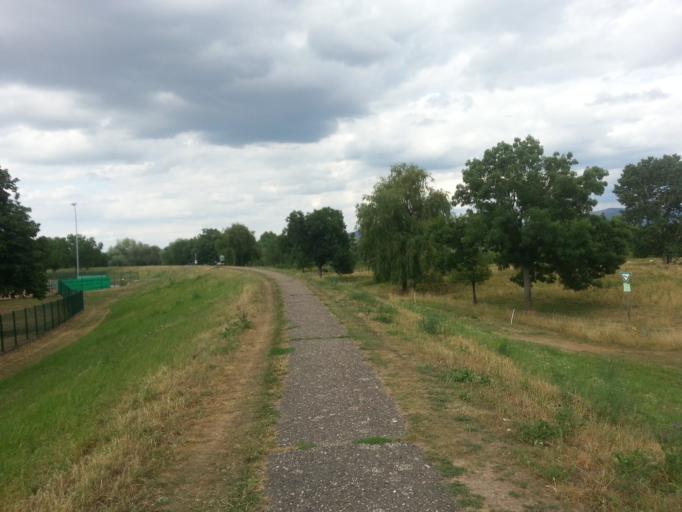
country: DE
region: Baden-Wuerttemberg
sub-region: Karlsruhe Region
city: Ilvesheim
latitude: 49.4670
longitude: 8.5709
